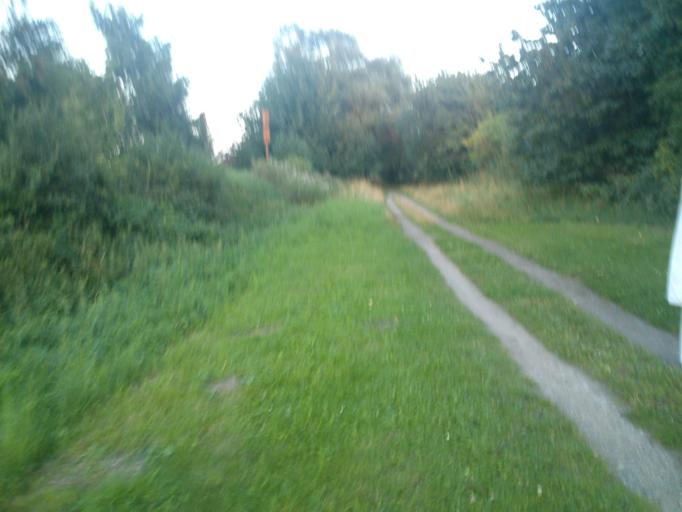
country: DK
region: South Denmark
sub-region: Fredericia Kommune
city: Fredericia
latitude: 55.5749
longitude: 9.7155
